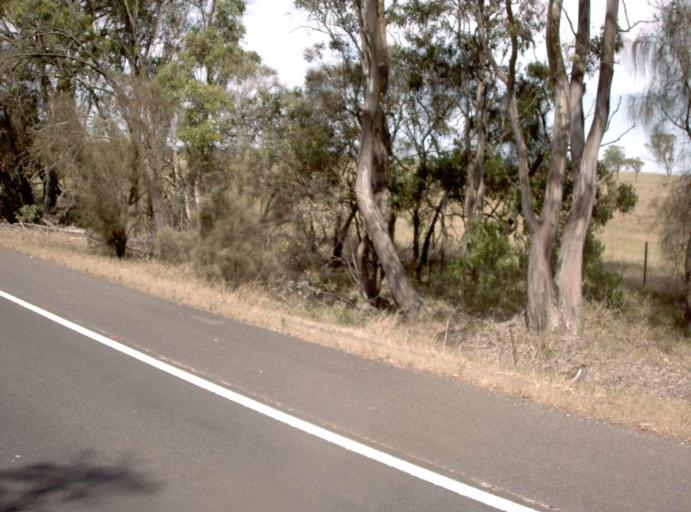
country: AU
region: Victoria
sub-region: Wellington
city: Sale
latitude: -37.9492
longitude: 147.1154
